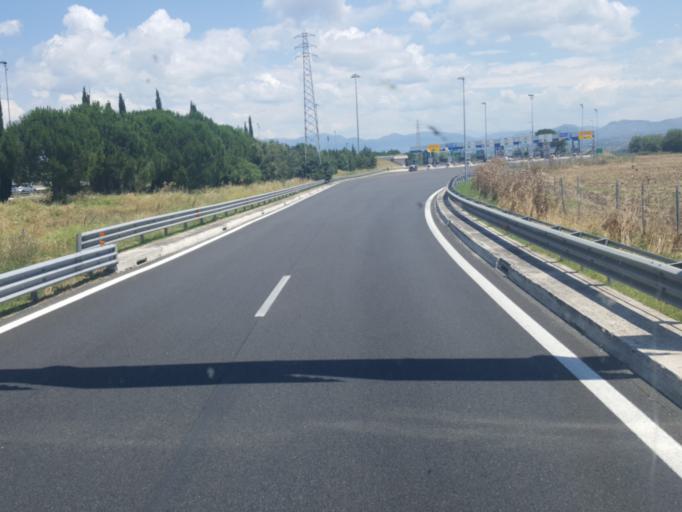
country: IT
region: Latium
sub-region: Citta metropolitana di Roma Capitale
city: Fiano Romano
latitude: 42.1380
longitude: 12.6049
